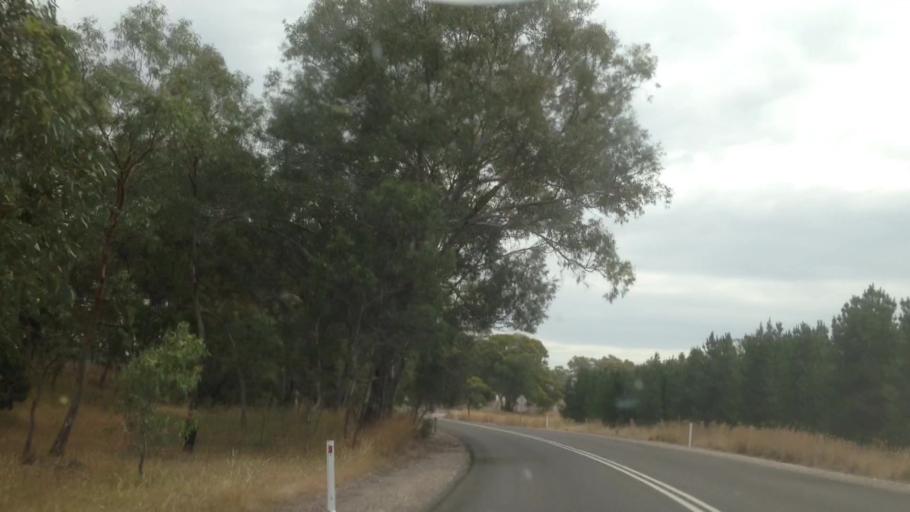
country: AU
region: South Australia
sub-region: Barossa
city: Williamstown
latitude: -34.6865
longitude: 138.9735
